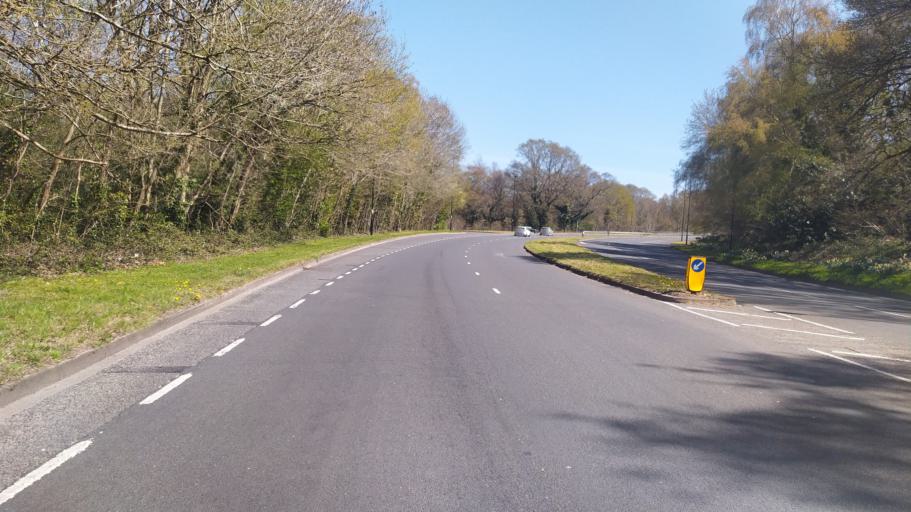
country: GB
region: England
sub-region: Southampton
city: Southampton
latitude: 50.9431
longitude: -1.4356
